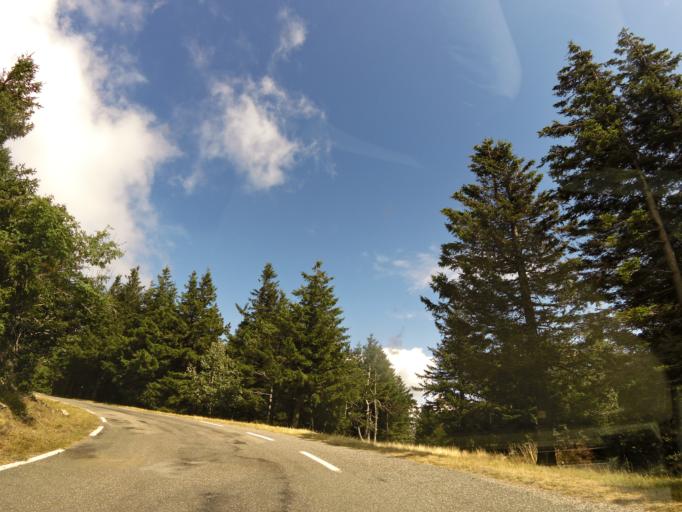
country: FR
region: Languedoc-Roussillon
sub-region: Departement du Gard
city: Valleraugue
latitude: 44.1168
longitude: 3.5705
